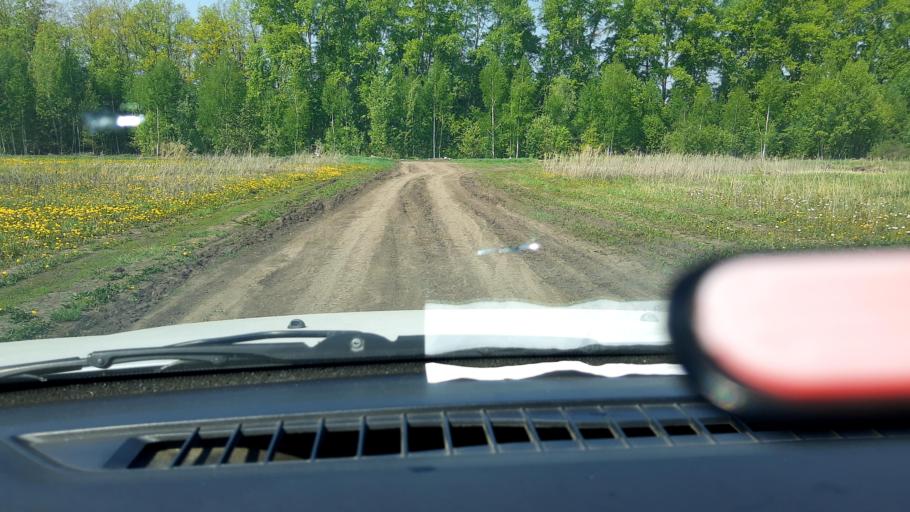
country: RU
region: Bashkortostan
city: Kabakovo
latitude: 54.6983
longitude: 56.1732
